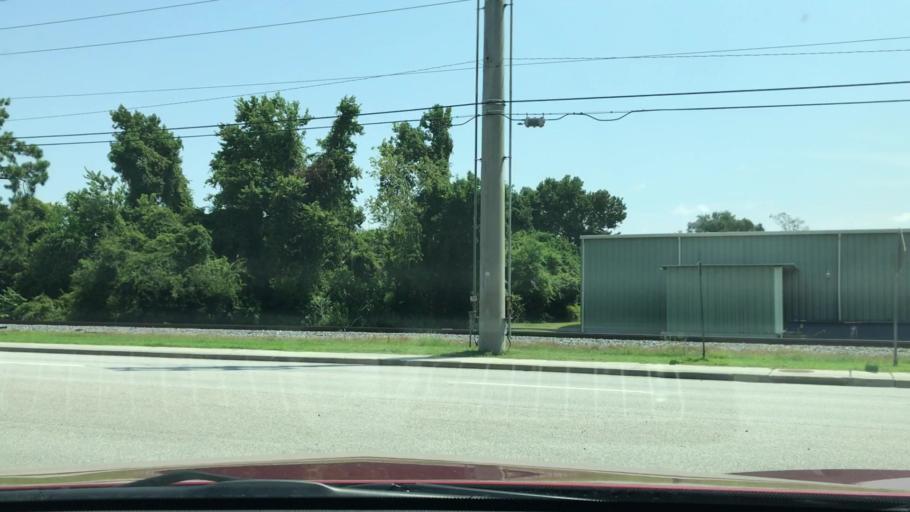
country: US
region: South Carolina
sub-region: Charleston County
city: North Charleston
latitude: 32.8825
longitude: -79.9741
